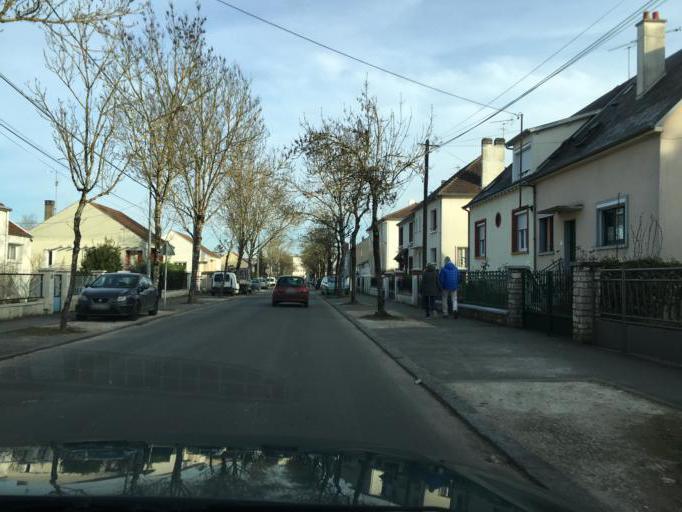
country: FR
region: Centre
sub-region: Departement du Loiret
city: Saint-Jean-le-Blanc
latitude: 47.8881
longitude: 1.9094
